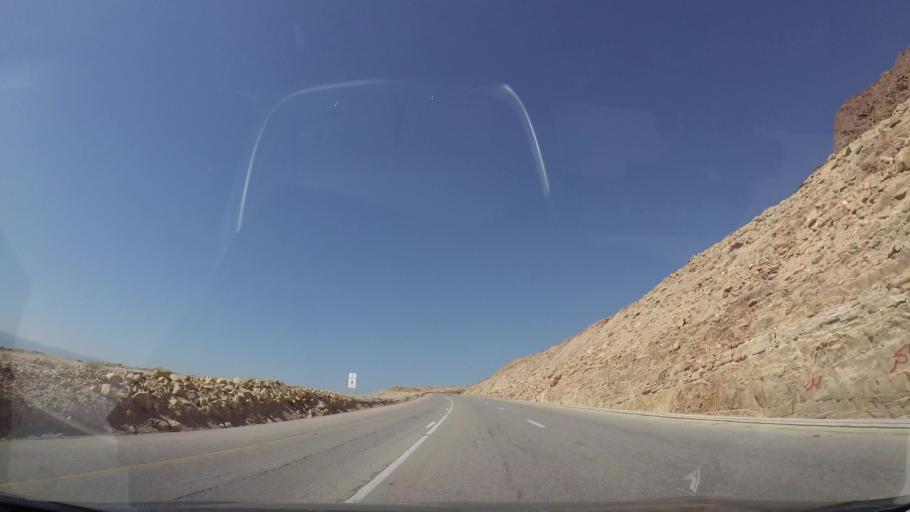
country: JO
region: Karak
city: Al Qasr
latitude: 31.4974
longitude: 35.5645
